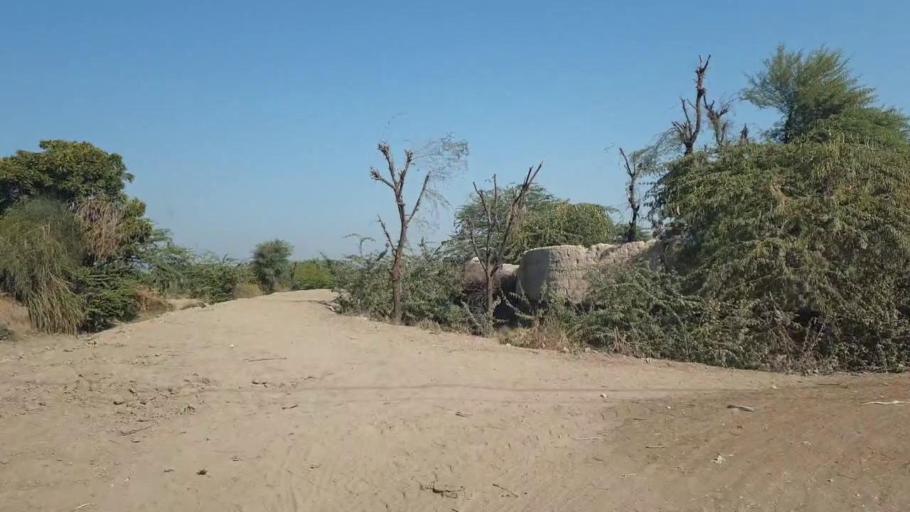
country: PK
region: Sindh
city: Shahpur Chakar
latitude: 26.0828
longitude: 68.6050
